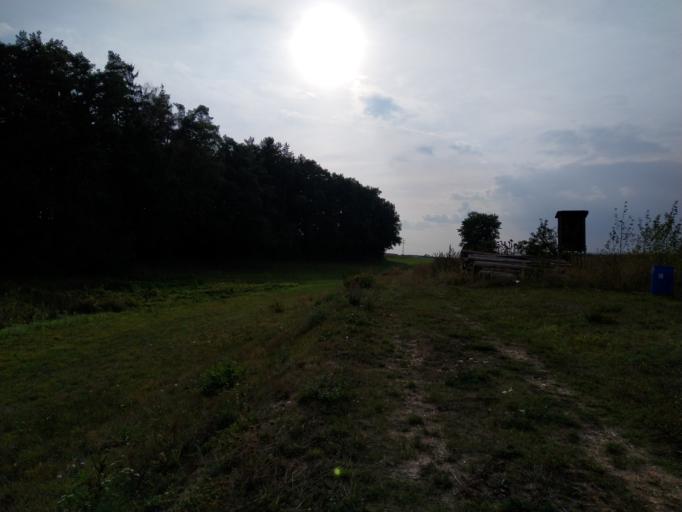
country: DE
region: Bavaria
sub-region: Regierungsbezirk Mittelfranken
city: Hagenbuchach
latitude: 49.5322
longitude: 10.7818
